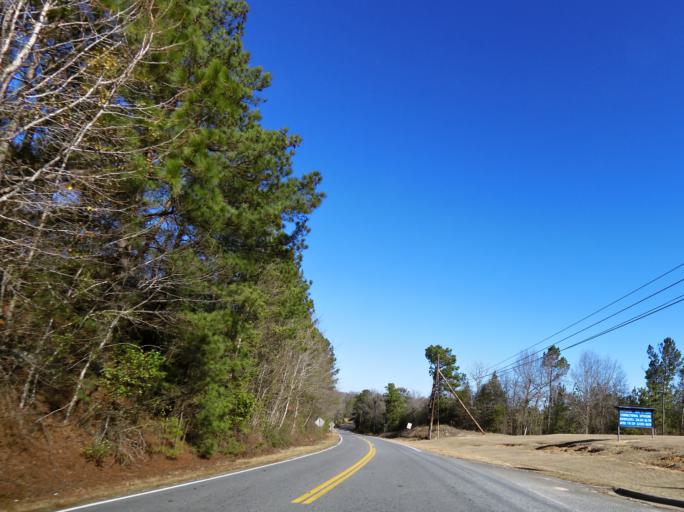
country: US
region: Georgia
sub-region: Bibb County
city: West Point
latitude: 32.7781
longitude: -83.7551
